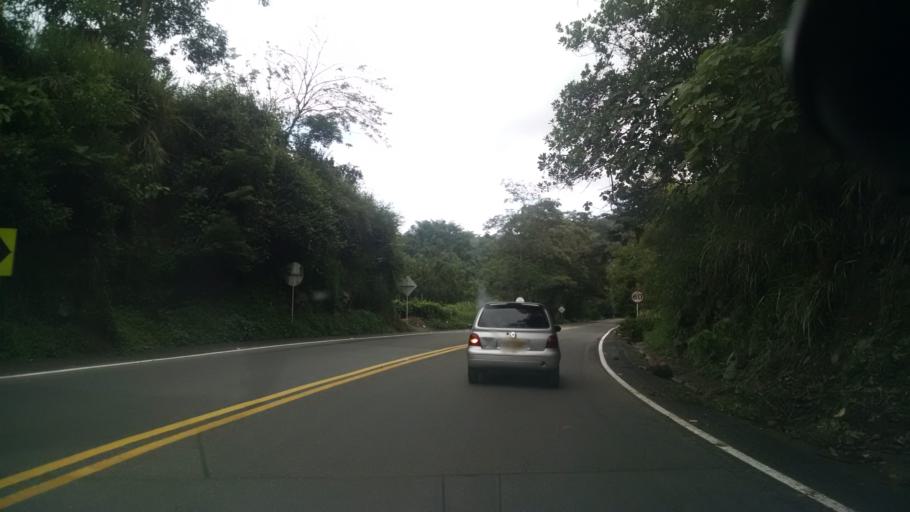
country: CO
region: Caldas
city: Palestina
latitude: 5.0398
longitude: -75.5993
